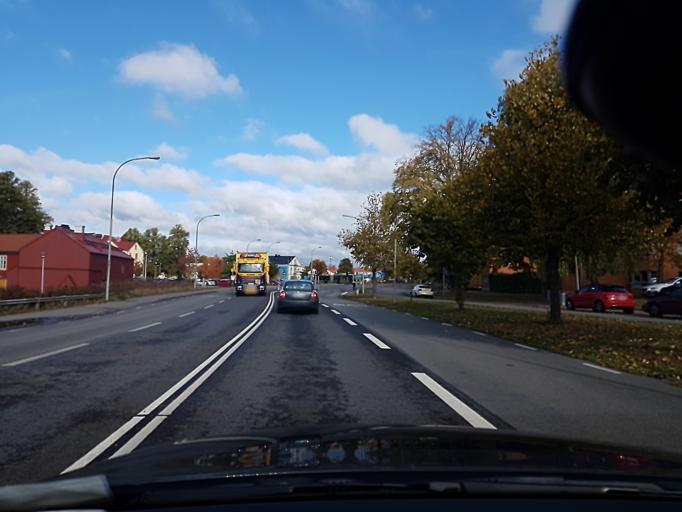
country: SE
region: Kronoberg
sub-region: Vaxjo Kommun
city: Vaexjoe
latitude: 56.8767
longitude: 14.8150
